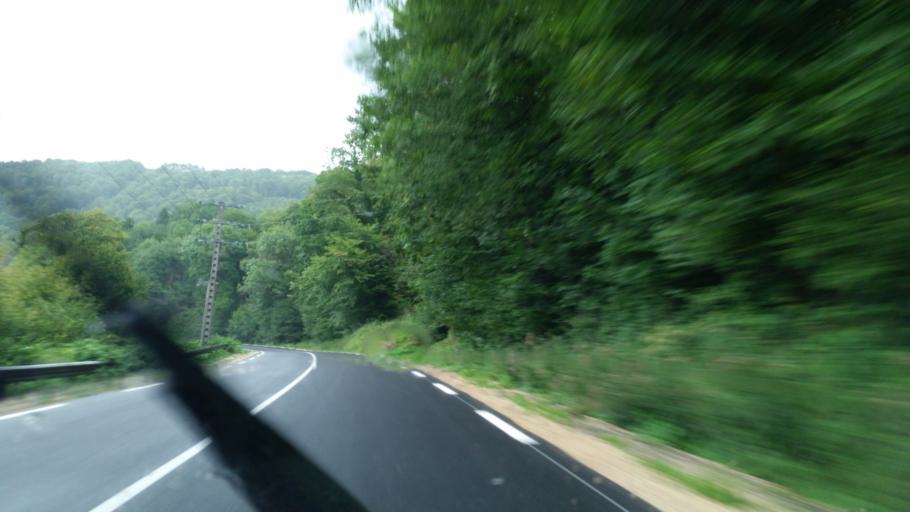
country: FR
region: Franche-Comte
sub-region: Departement du Doubs
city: Pont-de-Roide
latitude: 47.3761
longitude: 6.7688
